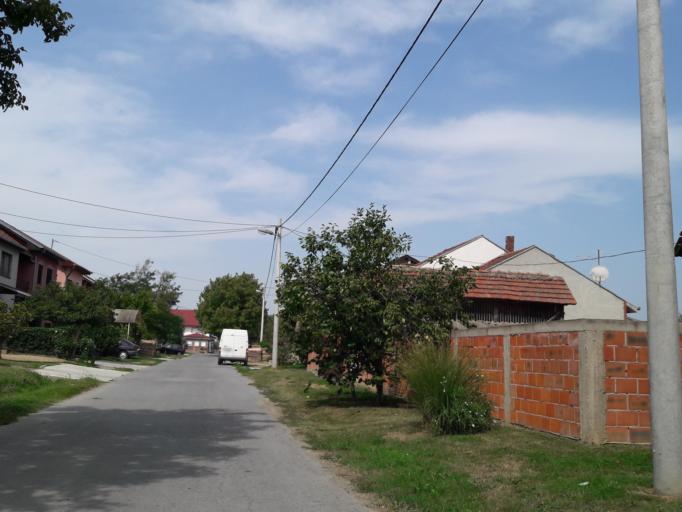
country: HR
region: Osjecko-Baranjska
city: Visnjevac
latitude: 45.5304
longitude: 18.6155
